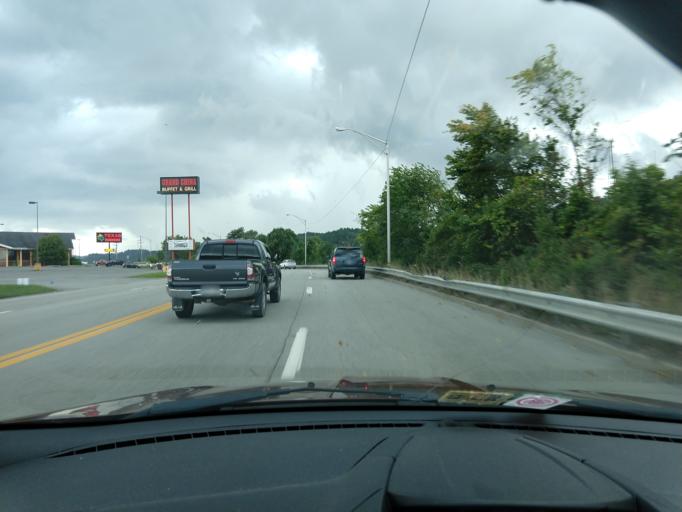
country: US
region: West Virginia
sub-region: Harrison County
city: Despard
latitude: 39.2760
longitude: -80.2833
